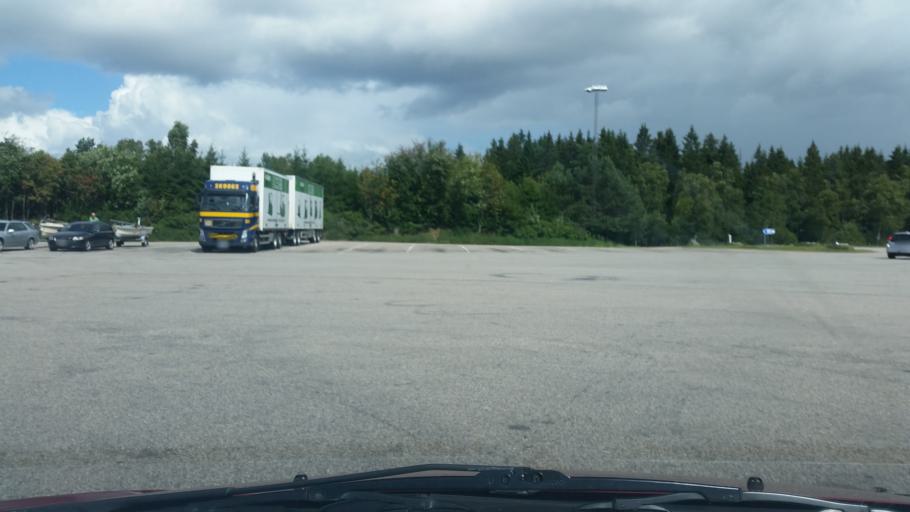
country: SE
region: Vaestra Goetaland
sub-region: Ulricehamns Kommun
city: Ulricehamn
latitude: 57.7799
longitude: 13.6614
